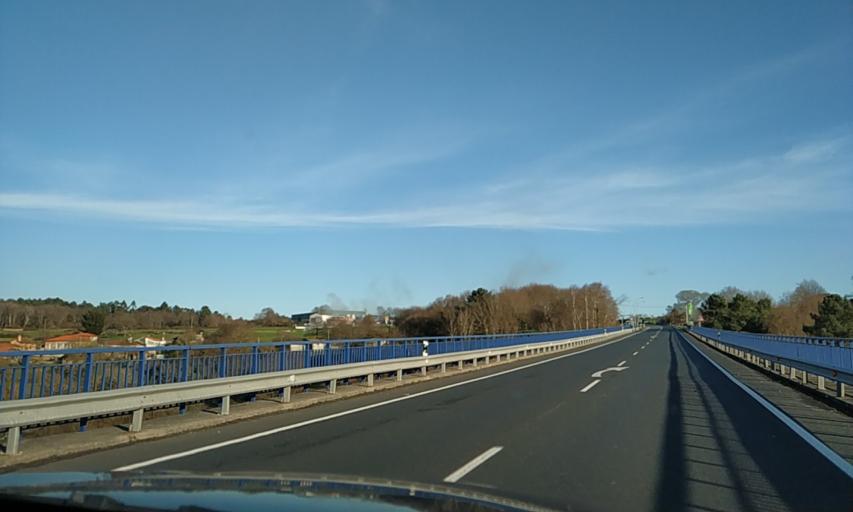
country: ES
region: Galicia
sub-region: Provincia de Pontevedra
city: Silleda
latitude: 42.6848
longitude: -8.1998
